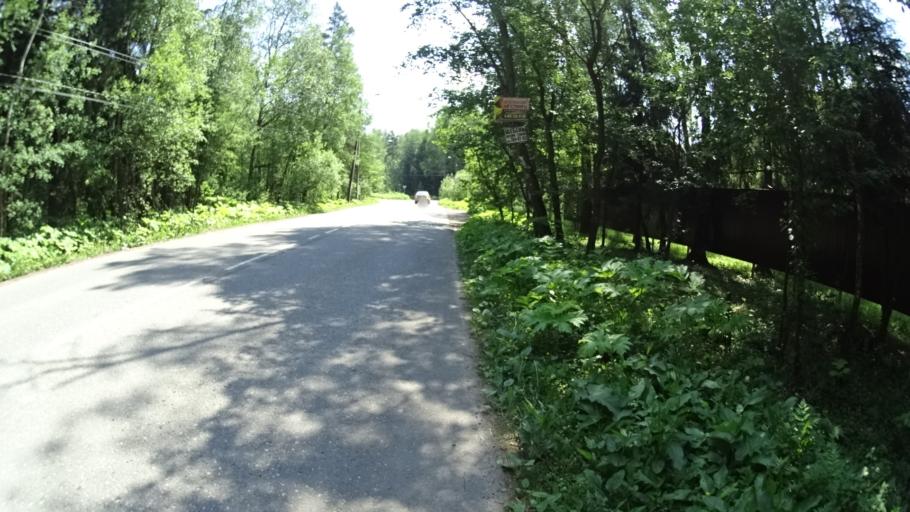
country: RU
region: Moskovskaya
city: Lesnoy
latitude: 56.0615
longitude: 38.0100
